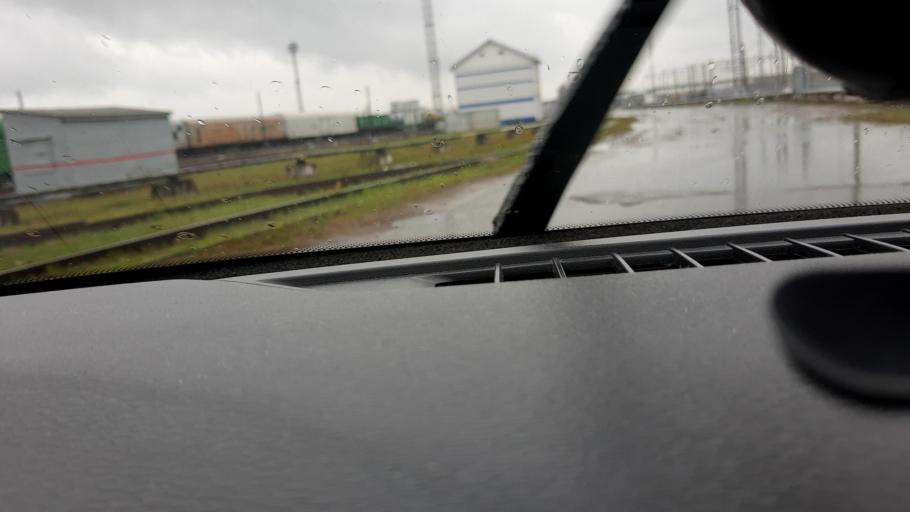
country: RU
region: Nizjnij Novgorod
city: Gorbatovka
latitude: 56.2843
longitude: 43.8493
